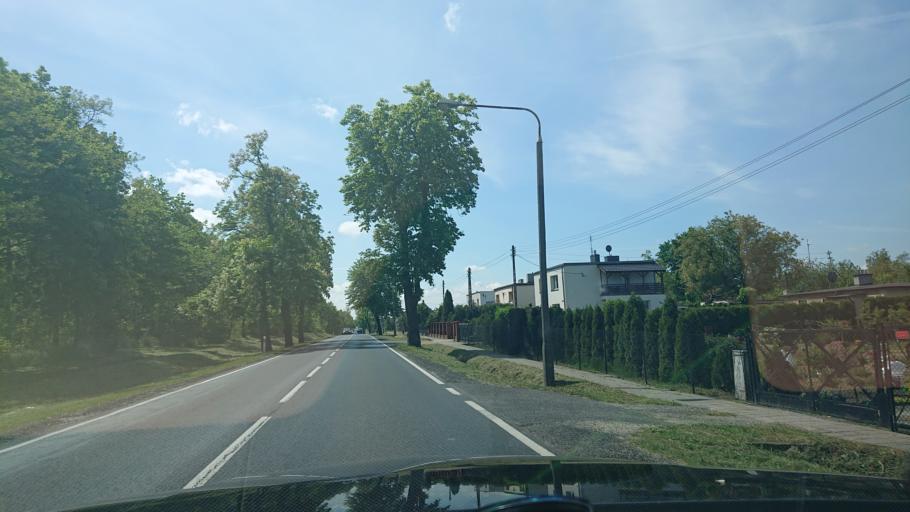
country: PL
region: Greater Poland Voivodeship
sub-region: Powiat gnieznienski
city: Gniezno
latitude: 52.5058
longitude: 17.5947
